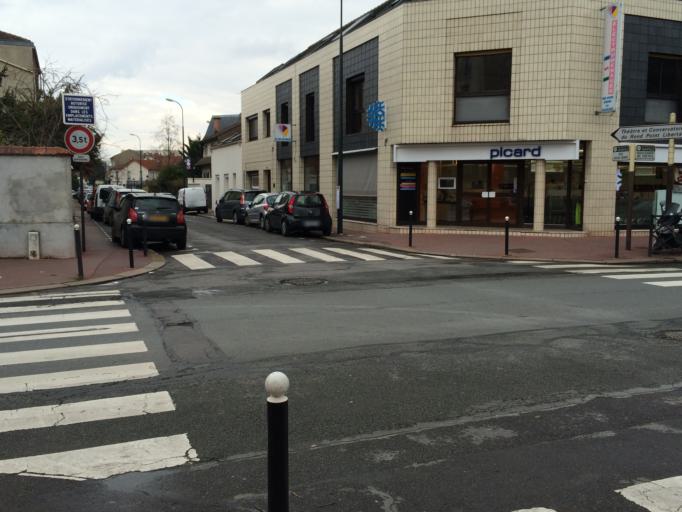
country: FR
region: Ile-de-France
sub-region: Departement du Val-de-Marne
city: Saint-Maur-des-Fosses
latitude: 48.7981
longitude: 2.4899
